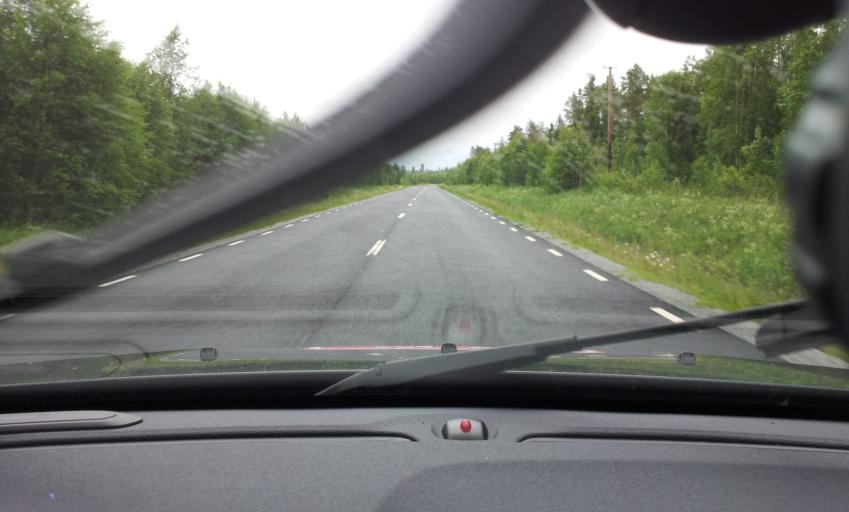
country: SE
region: Jaemtland
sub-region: OEstersunds Kommun
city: Lit
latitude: 63.7371
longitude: 14.7534
